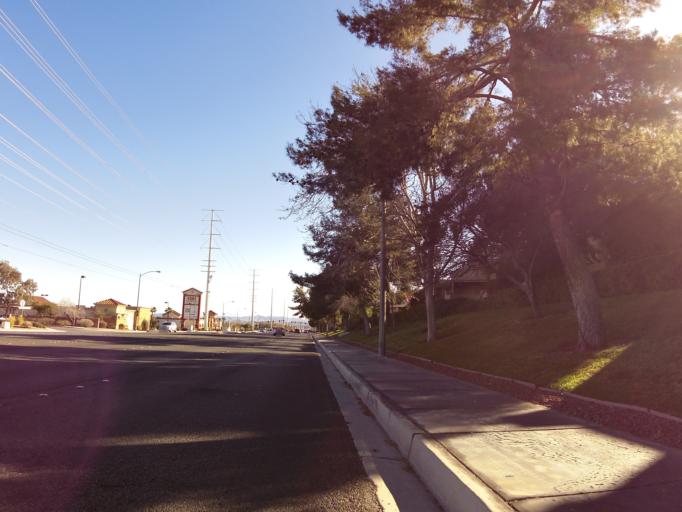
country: US
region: Nevada
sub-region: Clark County
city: Spring Valley
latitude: 36.1328
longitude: -115.2792
